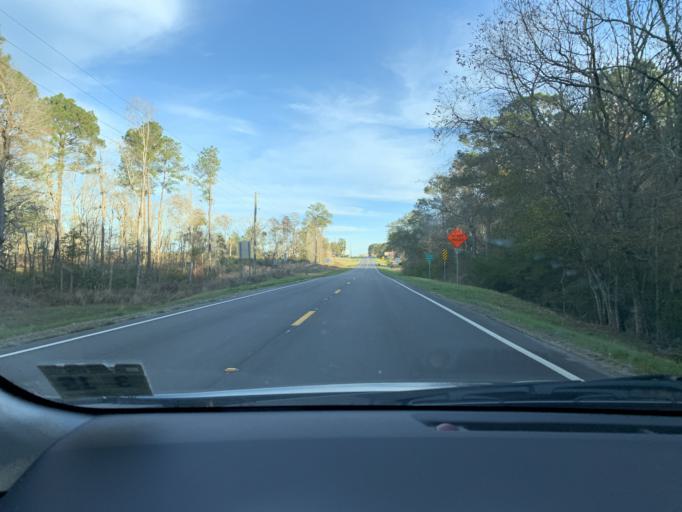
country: US
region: Georgia
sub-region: Coffee County
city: Broxton
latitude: 31.5801
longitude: -83.0604
